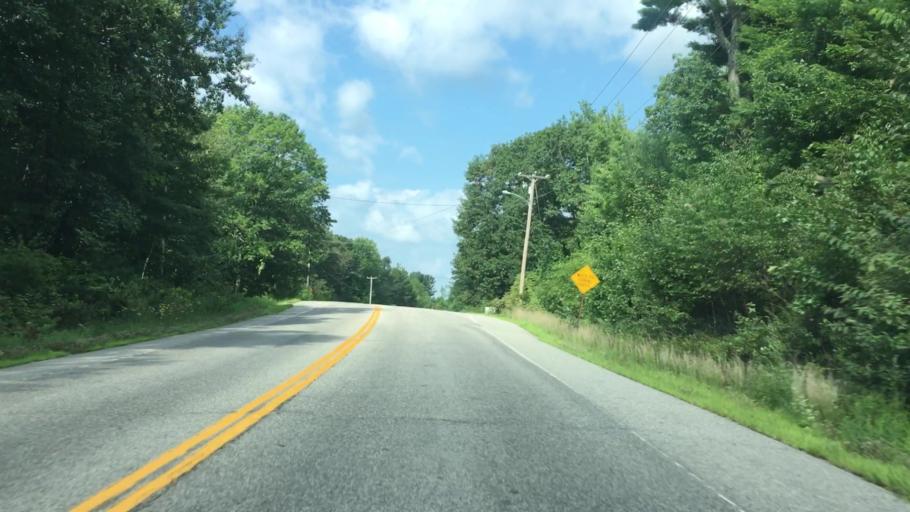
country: US
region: Maine
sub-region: Androscoggin County
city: Minot
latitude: 44.0285
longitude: -70.3266
